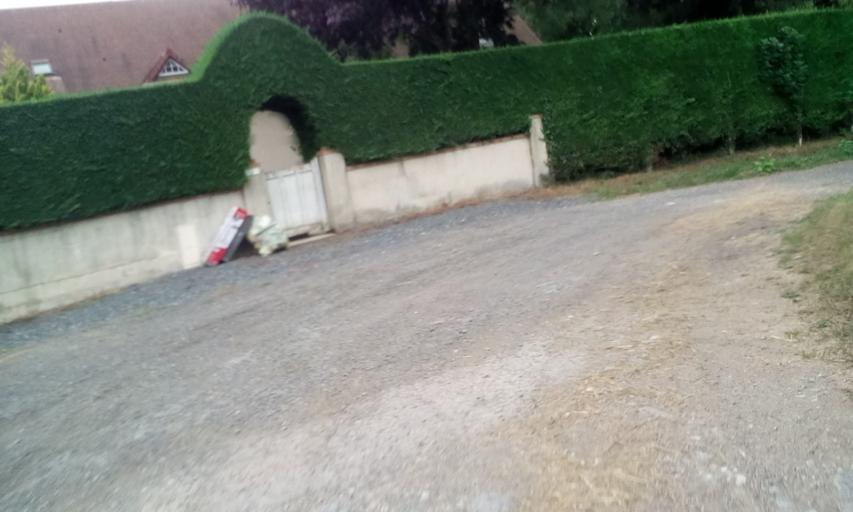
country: FR
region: Lower Normandy
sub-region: Departement du Calvados
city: Sannerville
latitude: 49.1855
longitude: -0.2125
